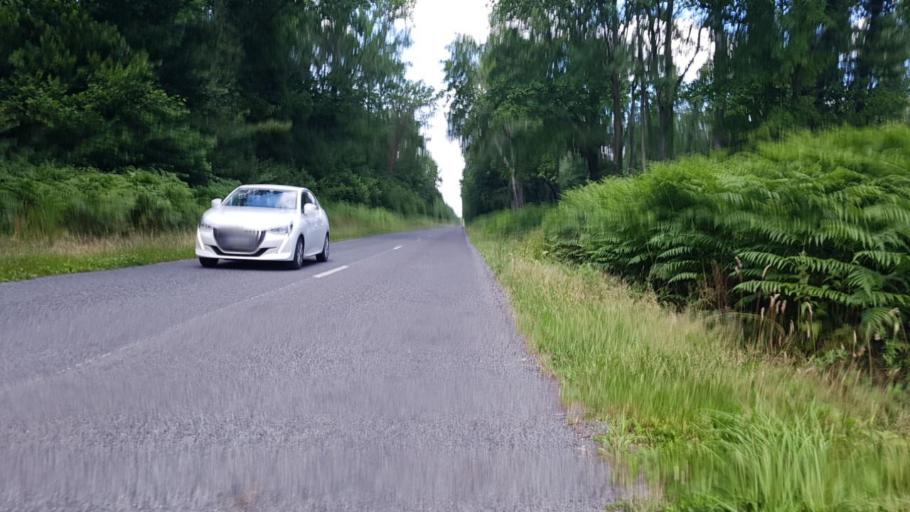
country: FR
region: Picardie
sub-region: Departement de l'Oise
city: Carlepont
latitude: 49.5123
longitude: 2.9833
